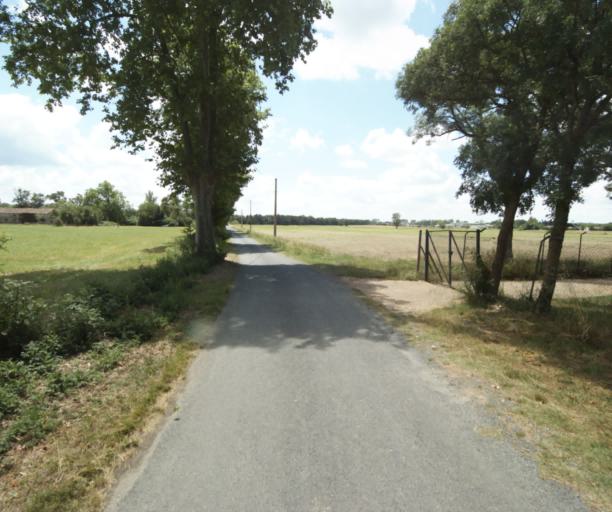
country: FR
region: Midi-Pyrenees
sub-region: Departement du Tarn
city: Puylaurens
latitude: 43.5196
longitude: 2.0220
